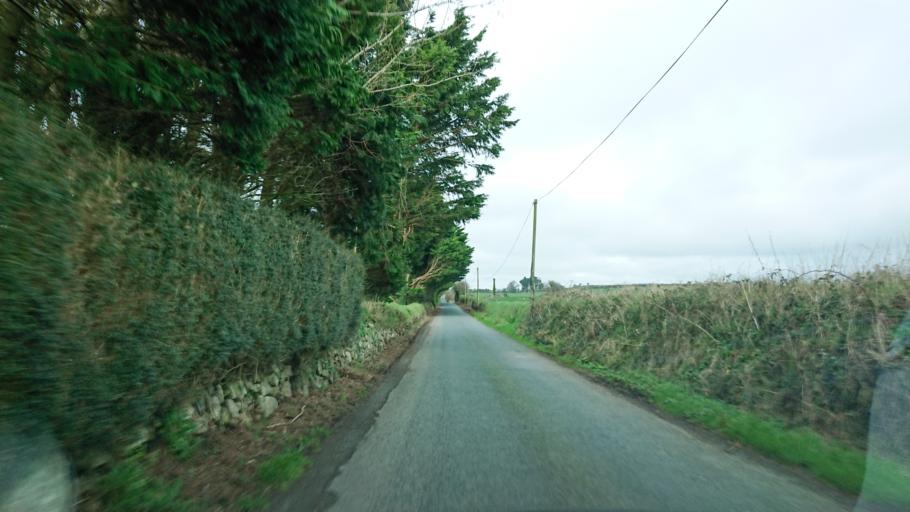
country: IE
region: Munster
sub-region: Waterford
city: Portlaw
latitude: 52.1652
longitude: -7.3057
